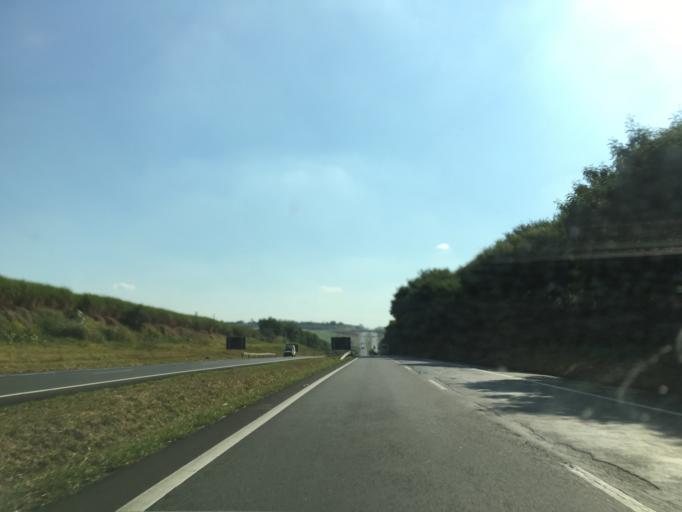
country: BR
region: Sao Paulo
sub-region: Piracicaba
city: Piracicaba
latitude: -22.7252
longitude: -47.5719
